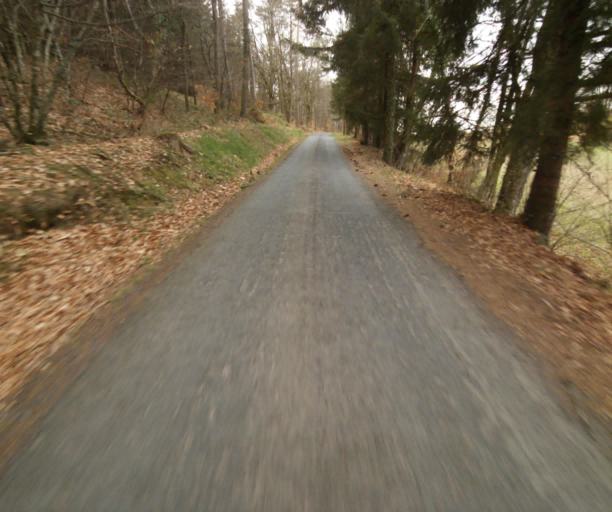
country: FR
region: Limousin
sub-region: Departement de la Correze
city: Treignac
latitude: 45.4476
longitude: 1.8198
